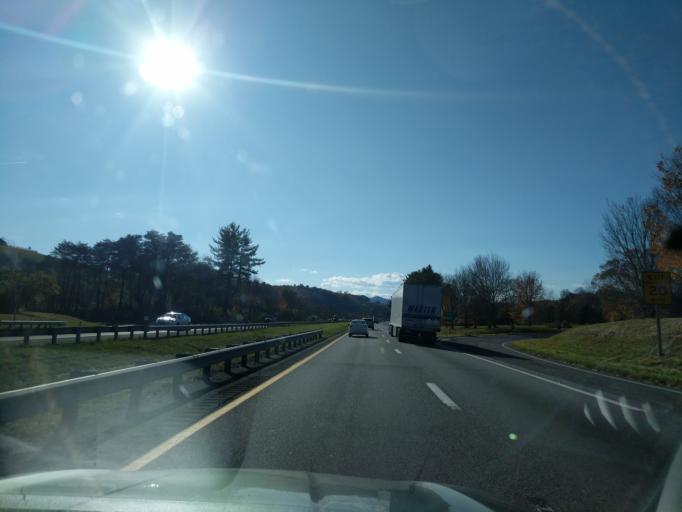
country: US
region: Virginia
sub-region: Pulaski County
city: Pulaski
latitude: 36.9937
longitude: -80.7930
